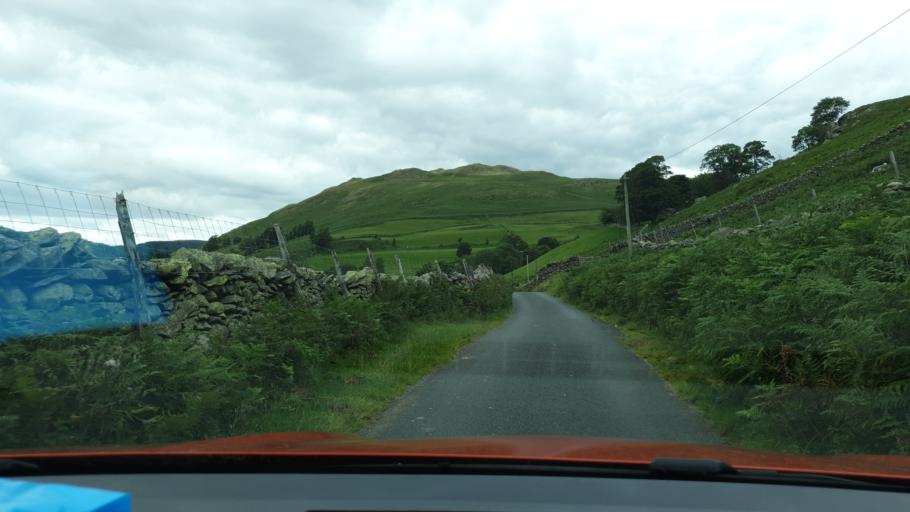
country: GB
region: England
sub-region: Cumbria
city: Ambleside
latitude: 54.5597
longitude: -2.8763
